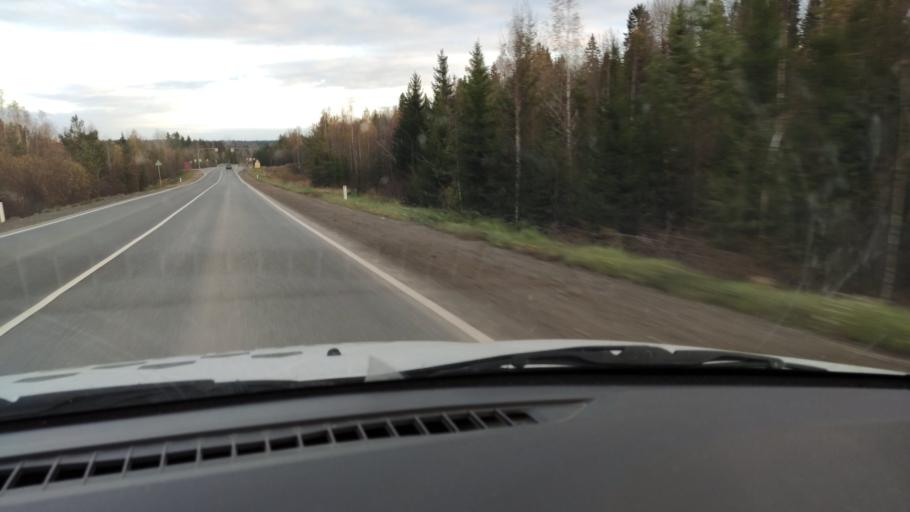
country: RU
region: Kirov
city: Omutninsk
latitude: 58.6988
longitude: 52.1192
